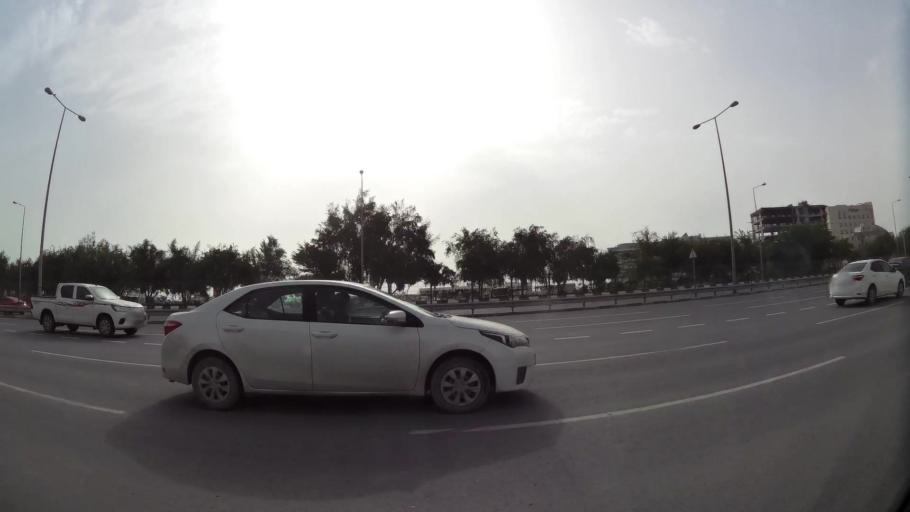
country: QA
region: Baladiyat ad Dawhah
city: Doha
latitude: 25.2707
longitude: 51.5518
